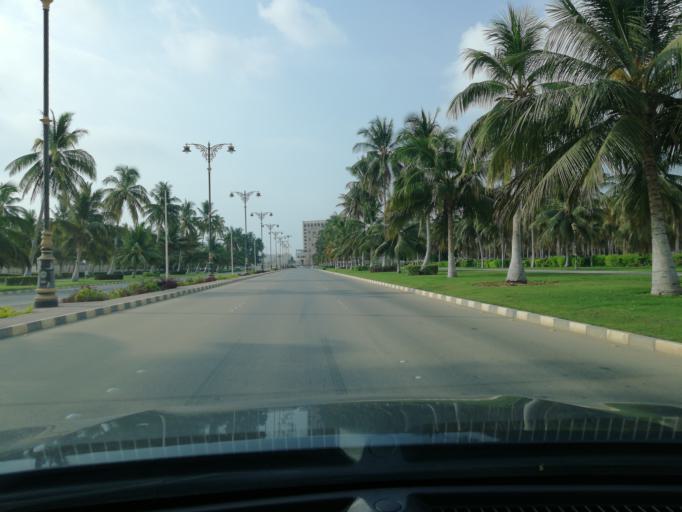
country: OM
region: Zufar
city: Salalah
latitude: 17.0281
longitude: 54.1106
